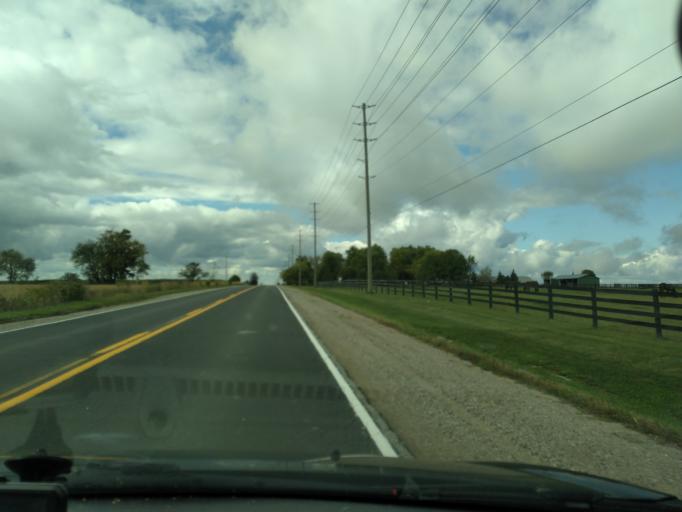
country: CA
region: Ontario
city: Innisfil
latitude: 44.2814
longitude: -79.6960
